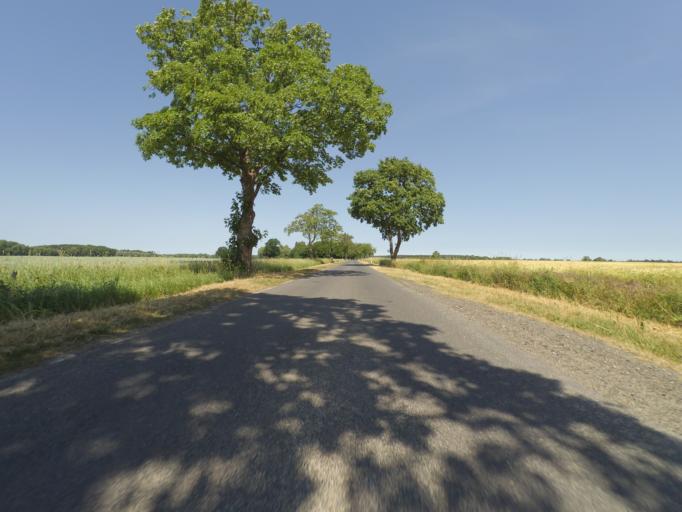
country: DE
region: Brandenburg
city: Gerdshagen
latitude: 53.2925
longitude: 12.2730
